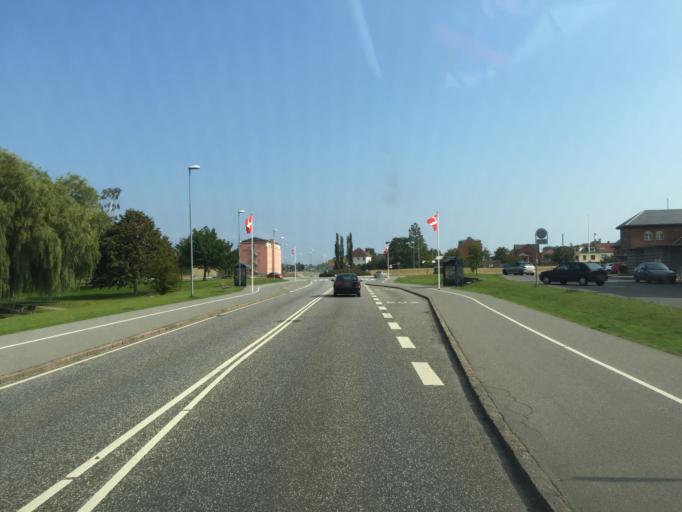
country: DK
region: South Denmark
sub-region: Nyborg Kommune
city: Nyborg
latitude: 55.3098
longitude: 10.7962
